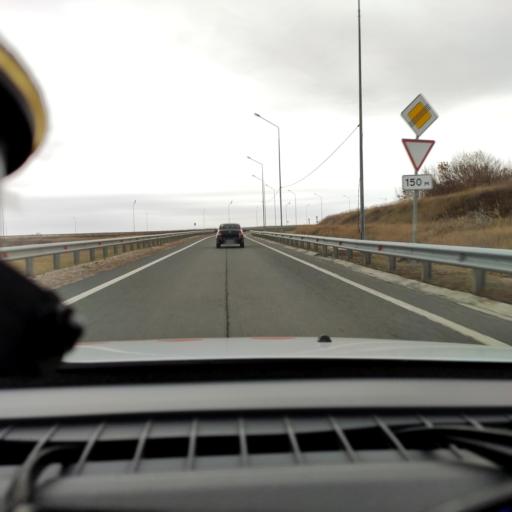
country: RU
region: Samara
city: Smyshlyayevka
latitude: 53.1473
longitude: 50.3901
